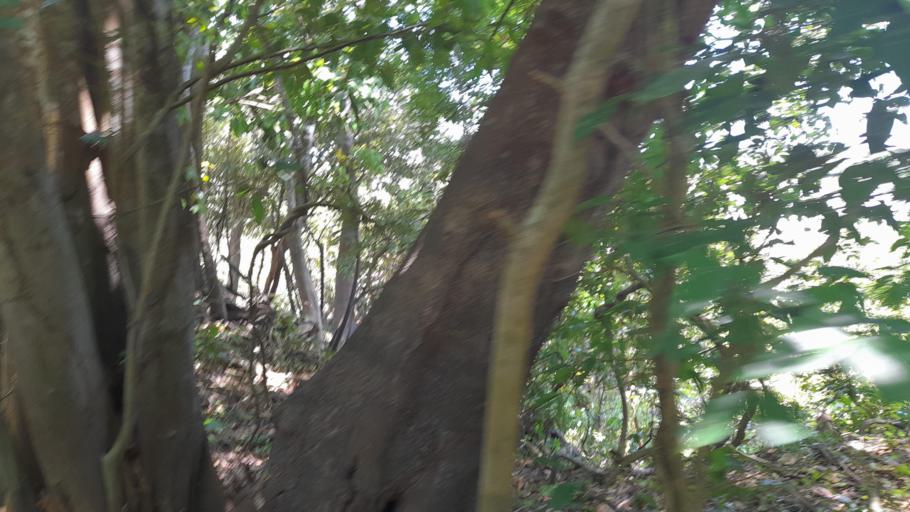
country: PE
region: Ucayali
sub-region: Provincia de Coronel Portillo
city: Puerto Callao
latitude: -8.2618
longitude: -74.6400
